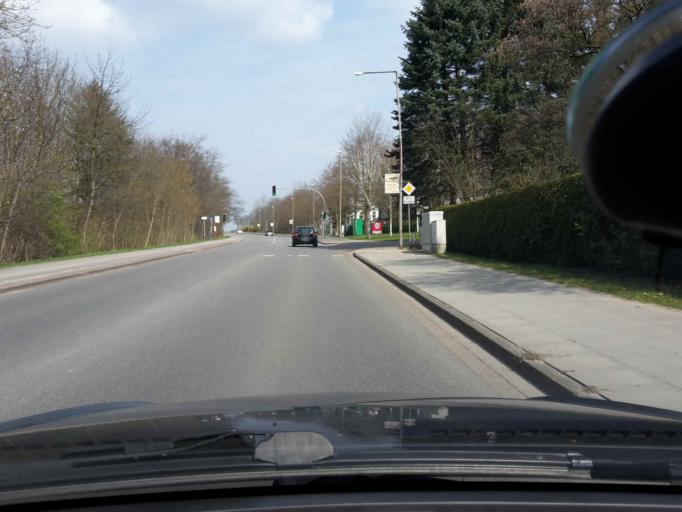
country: DE
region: Lower Saxony
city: Buchholz in der Nordheide
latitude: 53.3209
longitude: 9.8811
